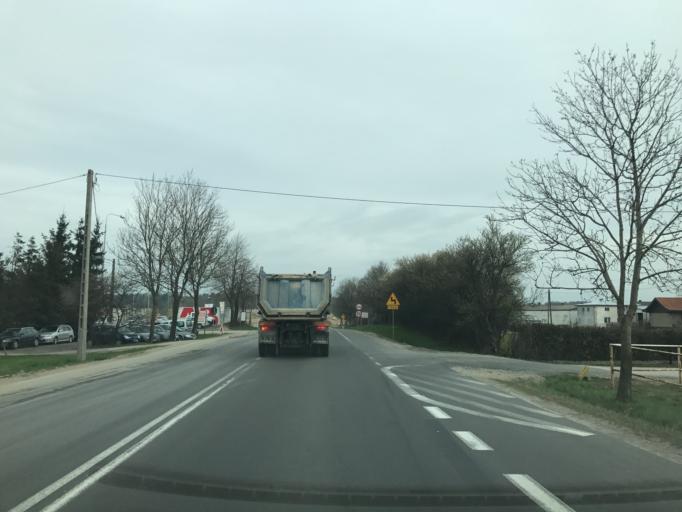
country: PL
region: Warmian-Masurian Voivodeship
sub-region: Powiat ostrodzki
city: Gierzwald
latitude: 53.5948
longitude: 20.0818
